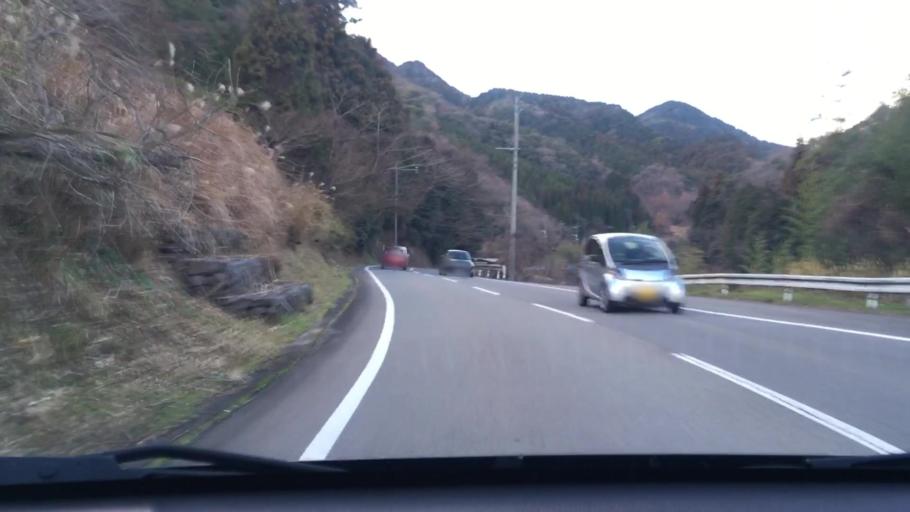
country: JP
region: Oita
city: Bungo-Takada-shi
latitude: 33.4685
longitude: 131.3876
